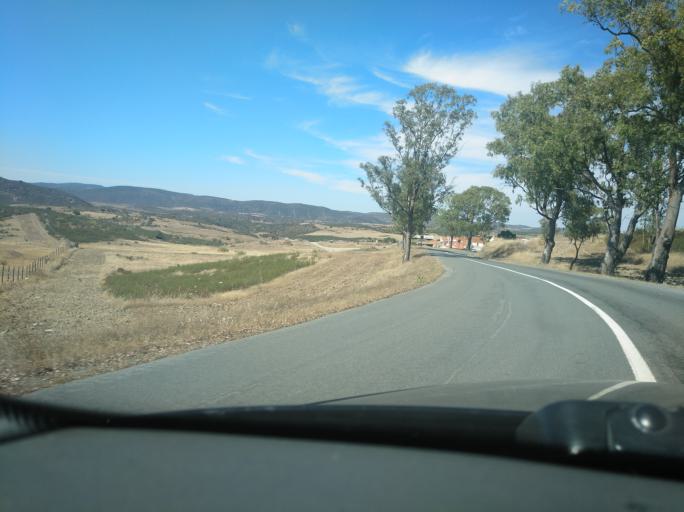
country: PT
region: Beja
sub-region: Mertola
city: Mertola
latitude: 37.6170
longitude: -7.7542
